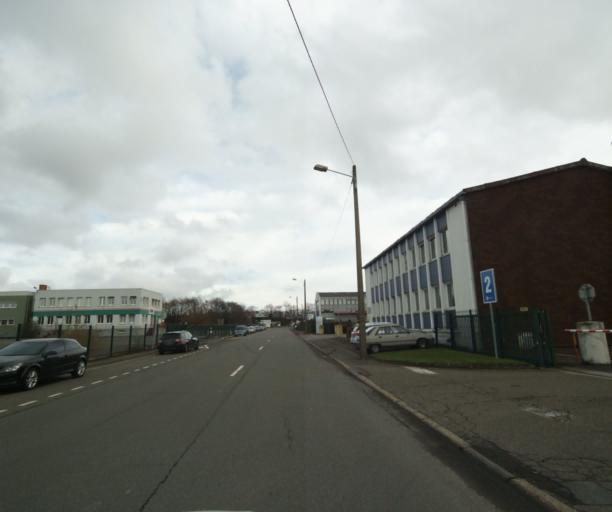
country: FR
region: Pays de la Loire
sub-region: Departement de la Sarthe
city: Allonnes
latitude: 47.9645
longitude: 0.1827
